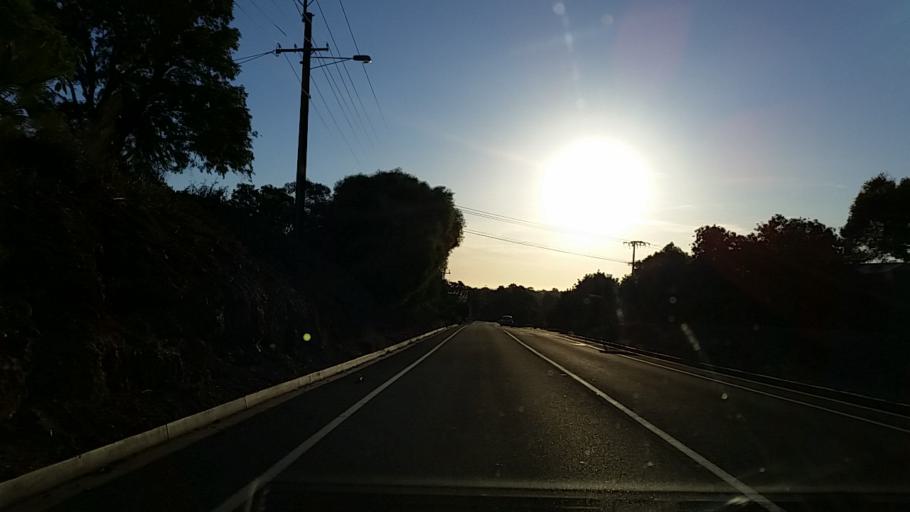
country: AU
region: South Australia
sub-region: Campbelltown
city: Athelstone
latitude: -34.8643
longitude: 138.7126
